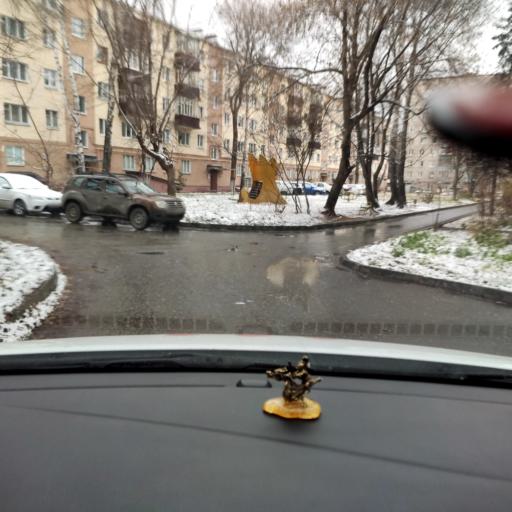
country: RU
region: Tatarstan
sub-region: Zelenodol'skiy Rayon
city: Zelenodolsk
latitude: 55.8445
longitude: 48.5081
